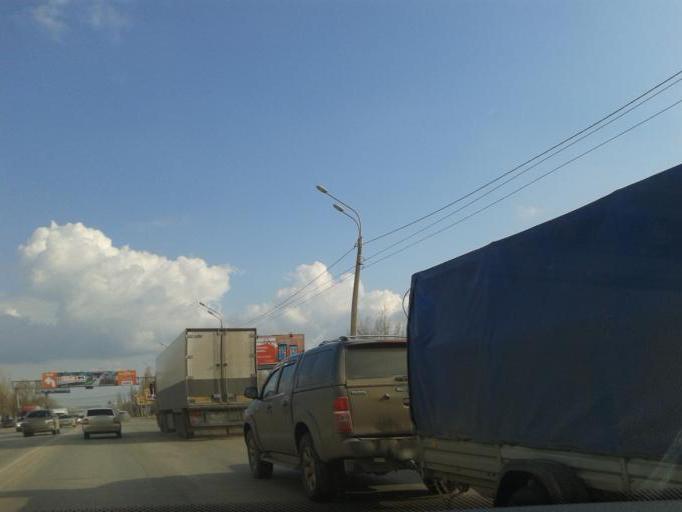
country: RU
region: Volgograd
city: Gorodishche
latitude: 48.7634
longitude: 44.4760
